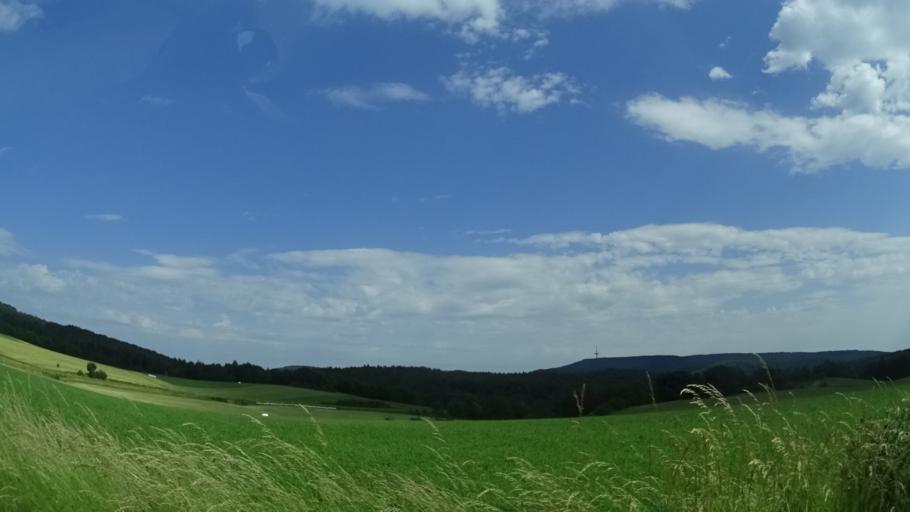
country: DE
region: Hesse
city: Haina
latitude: 51.0554
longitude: 8.9849
